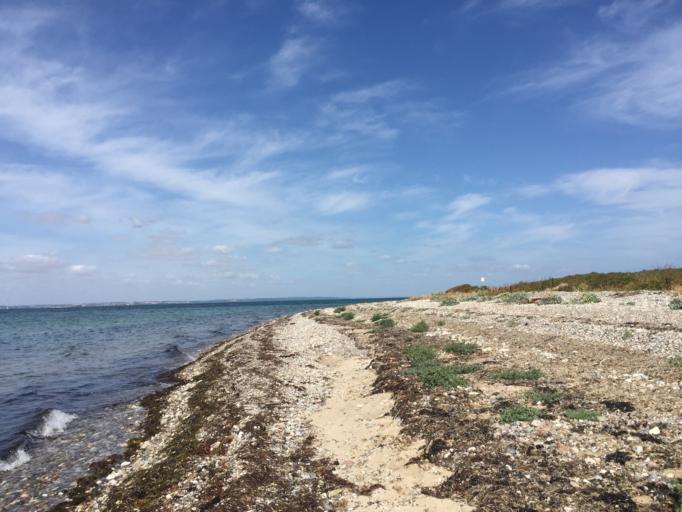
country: DK
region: Central Jutland
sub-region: Arhus Kommune
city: Beder
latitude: 55.9584
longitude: 10.4040
